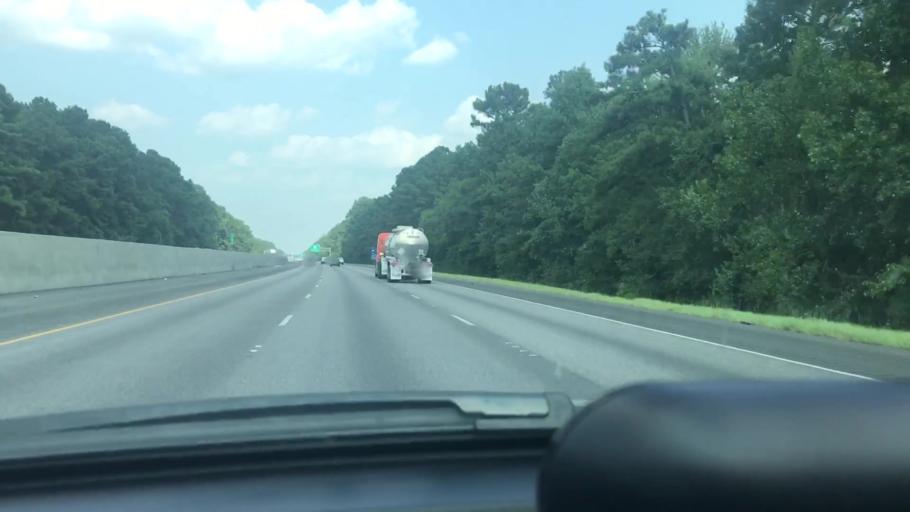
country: US
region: Louisiana
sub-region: Livingston Parish
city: Walker
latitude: 30.4667
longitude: -90.8887
